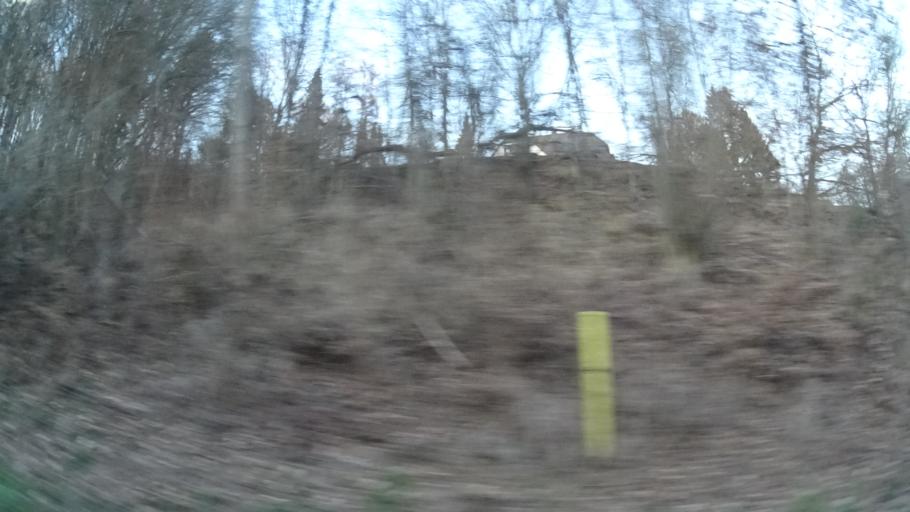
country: DE
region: Bavaria
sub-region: Regierungsbezirk Unterfranken
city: Mombris
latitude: 50.1002
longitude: 9.1210
